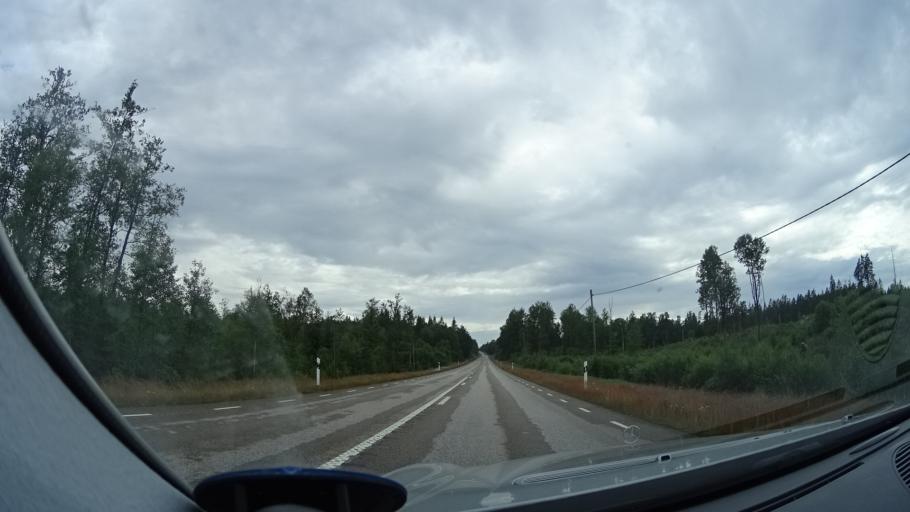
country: SE
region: Kronoberg
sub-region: Tingsryds Kommun
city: Tingsryd
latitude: 56.4445
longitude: 14.9827
